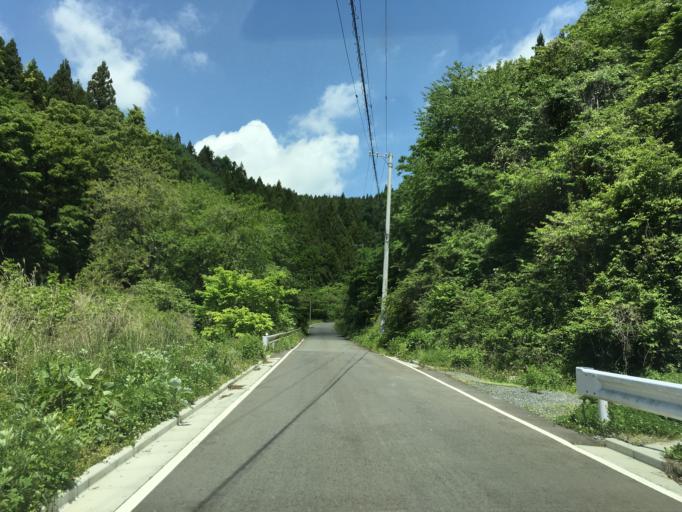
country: JP
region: Miyagi
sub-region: Oshika Gun
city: Onagawa Cho
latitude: 38.6734
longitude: 141.3470
